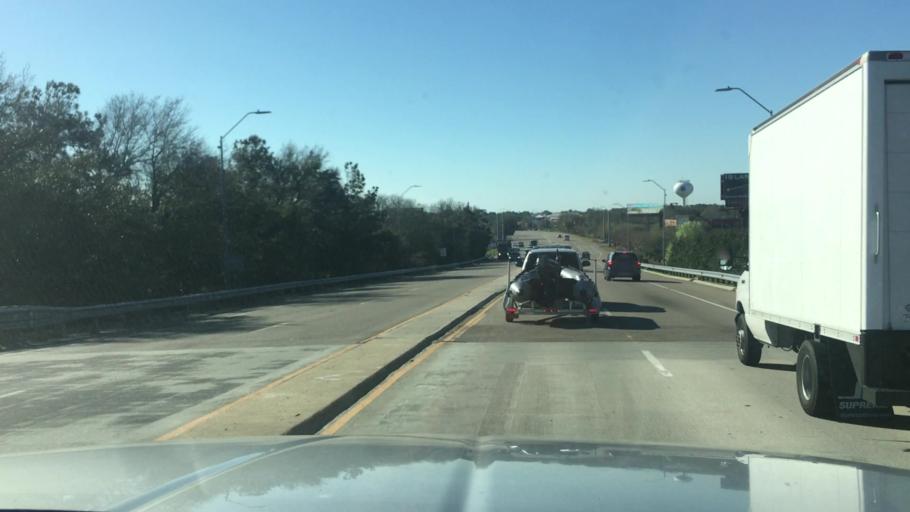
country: US
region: North Carolina
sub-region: New Hanover County
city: Sea Breeze
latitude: 34.0534
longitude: -77.8997
